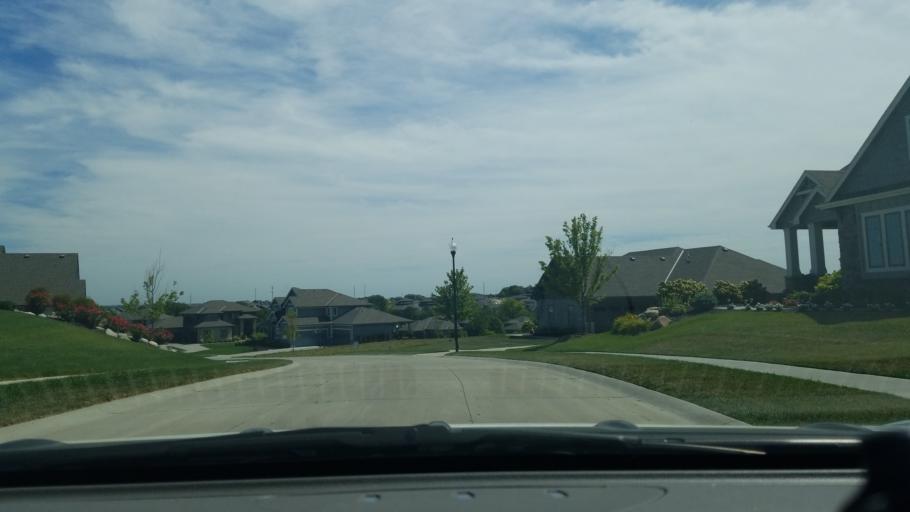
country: US
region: Nebraska
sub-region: Sarpy County
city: Chalco
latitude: 41.1413
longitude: -96.1050
